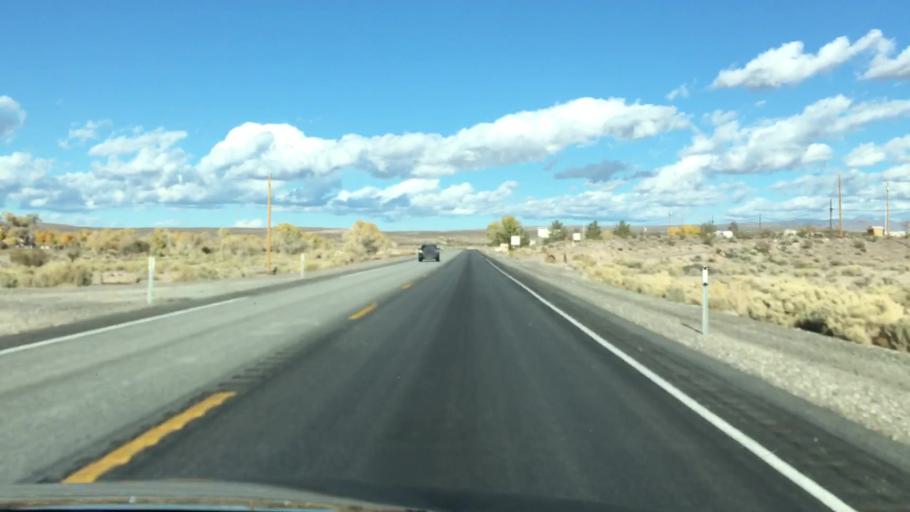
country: US
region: Nevada
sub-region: Nye County
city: Beatty
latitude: 36.9441
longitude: -116.7192
